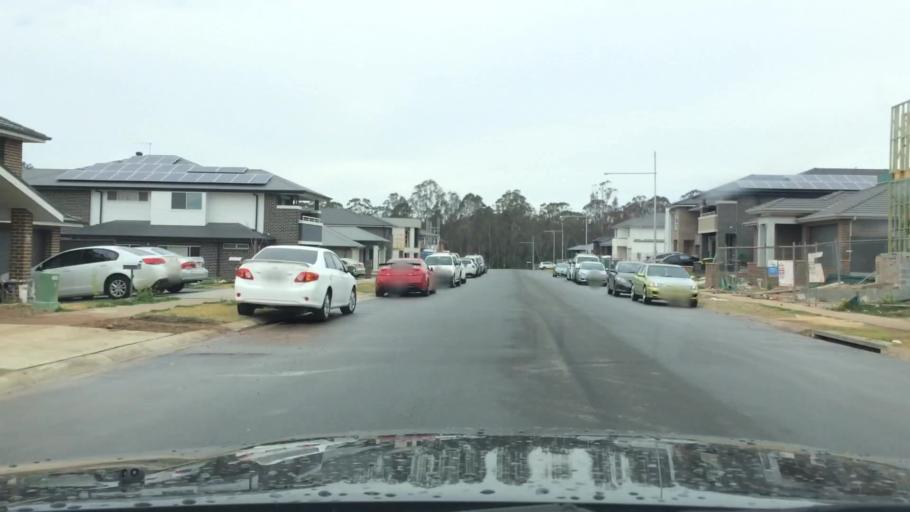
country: AU
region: New South Wales
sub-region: Campbelltown Municipality
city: Denham Court
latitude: -33.9554
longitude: 150.8451
